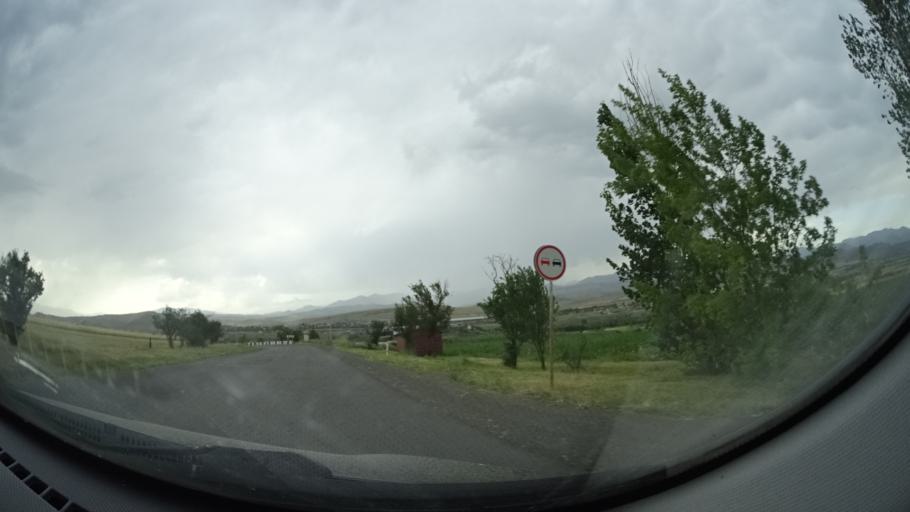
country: GE
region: Samtskhe-Javakheti
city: Akhaltsikhe
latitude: 41.6415
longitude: 43.0273
